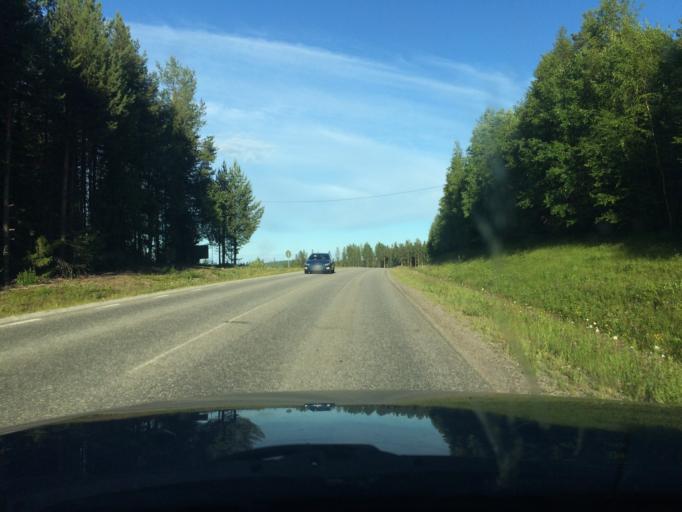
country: SE
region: Norrbotten
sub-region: Pitea Kommun
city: Roknas
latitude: 65.3192
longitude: 21.2816
